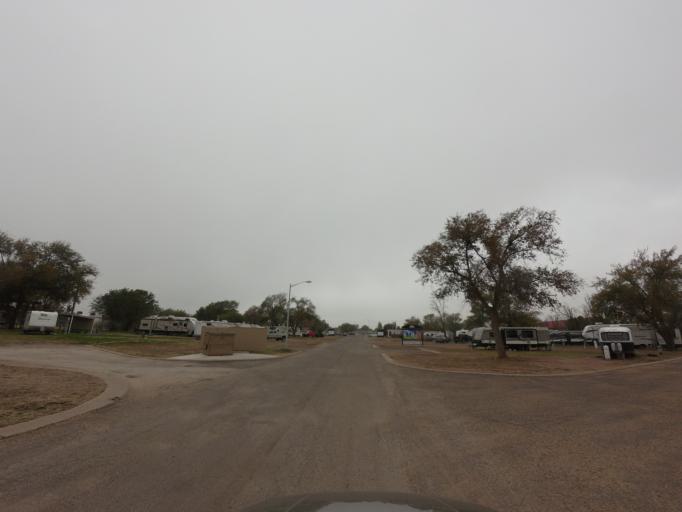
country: US
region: New Mexico
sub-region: Curry County
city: Clovis
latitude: 34.4293
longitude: -103.1944
